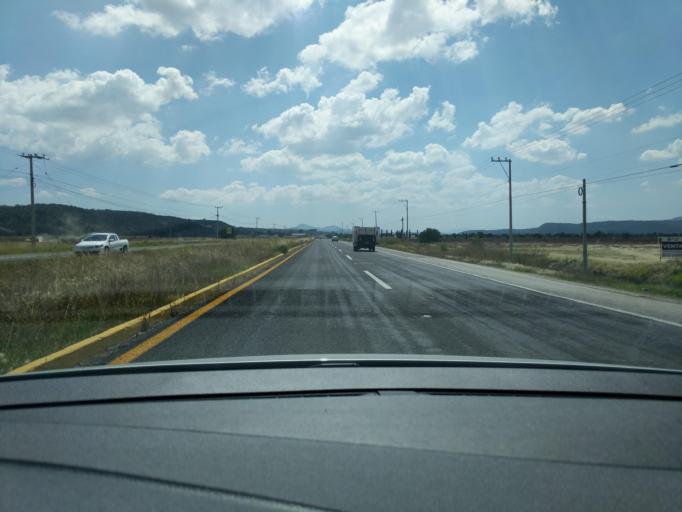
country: MX
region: Hidalgo
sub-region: Mineral de la Reforma
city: Rinconada de los Angeles
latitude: 20.0092
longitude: -98.7158
